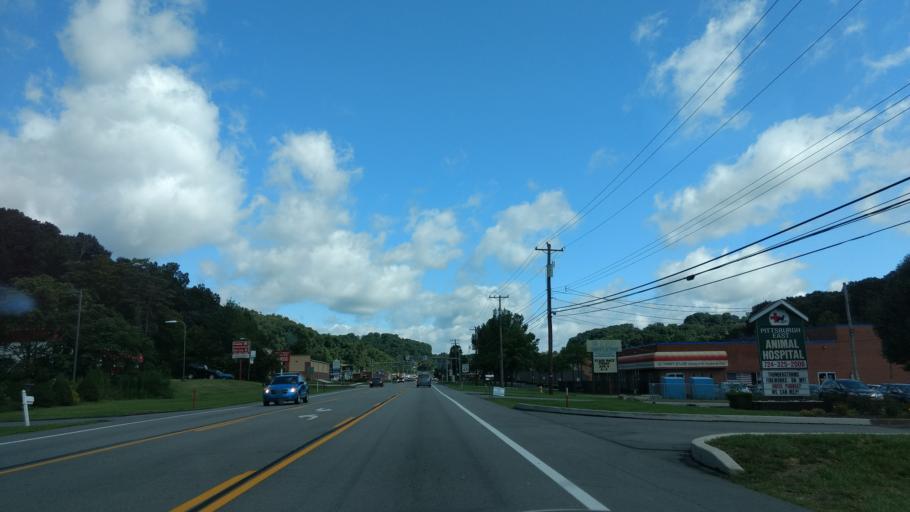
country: US
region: Pennsylvania
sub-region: Westmoreland County
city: Murrysville
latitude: 40.4404
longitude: -79.7130
